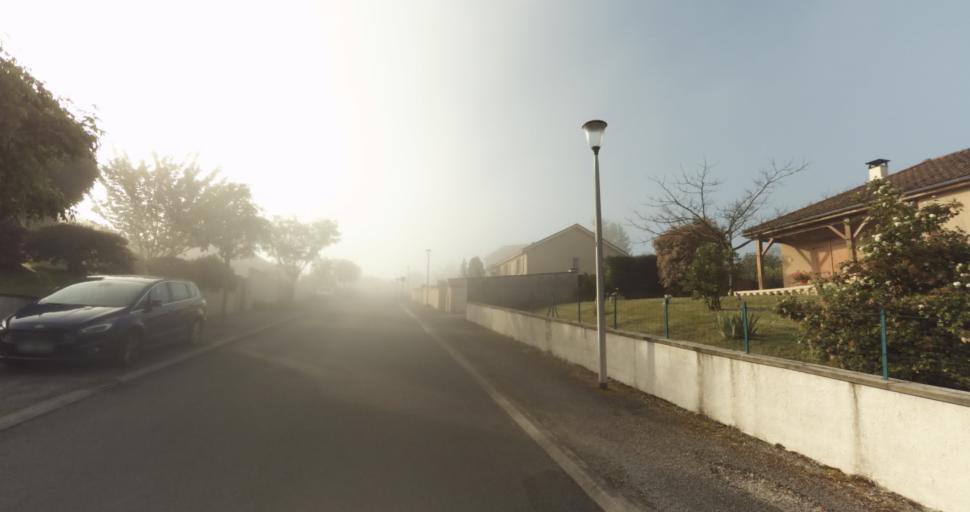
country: FR
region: Limousin
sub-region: Departement de la Haute-Vienne
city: Condat-sur-Vienne
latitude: 45.7840
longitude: 1.2819
